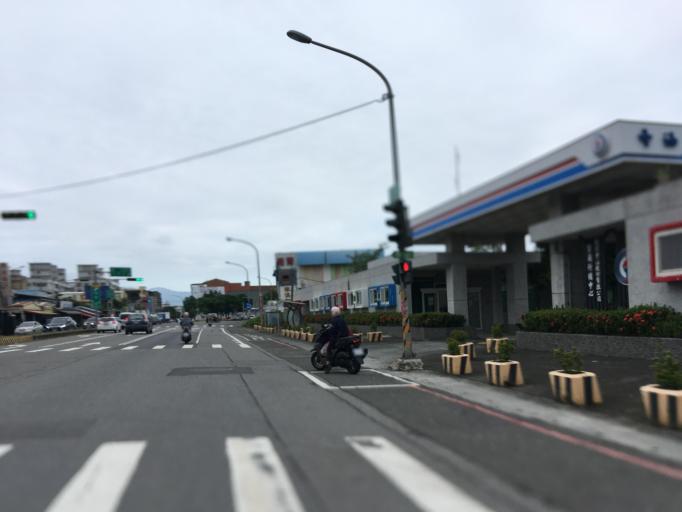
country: TW
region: Taiwan
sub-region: Yilan
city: Yilan
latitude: 24.6979
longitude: 121.7690
